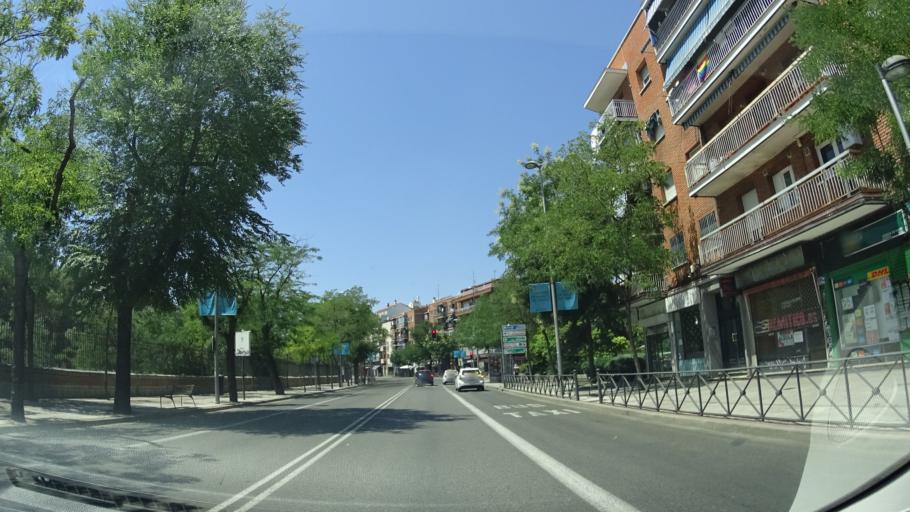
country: ES
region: Madrid
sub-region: Provincia de Madrid
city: Latina
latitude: 40.3849
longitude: -3.7386
